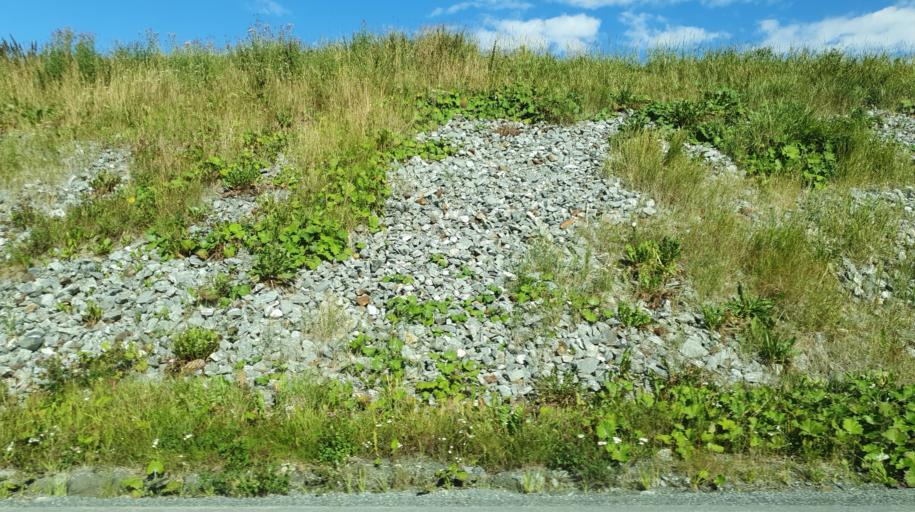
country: NO
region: Nord-Trondelag
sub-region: Levanger
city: Skogn
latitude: 63.6984
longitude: 11.2534
